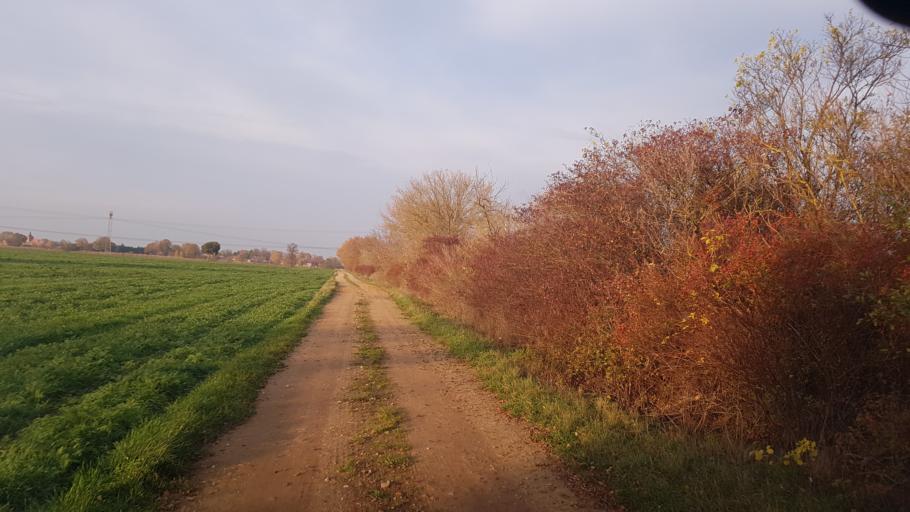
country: DE
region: Brandenburg
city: Schonewalde
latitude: 51.6492
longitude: 13.5993
